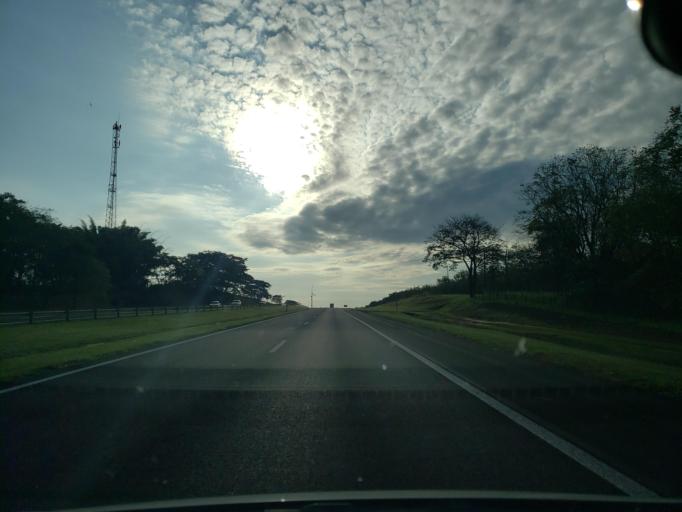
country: BR
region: Sao Paulo
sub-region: Valparaiso
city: Valparaiso
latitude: -21.1727
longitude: -50.9308
